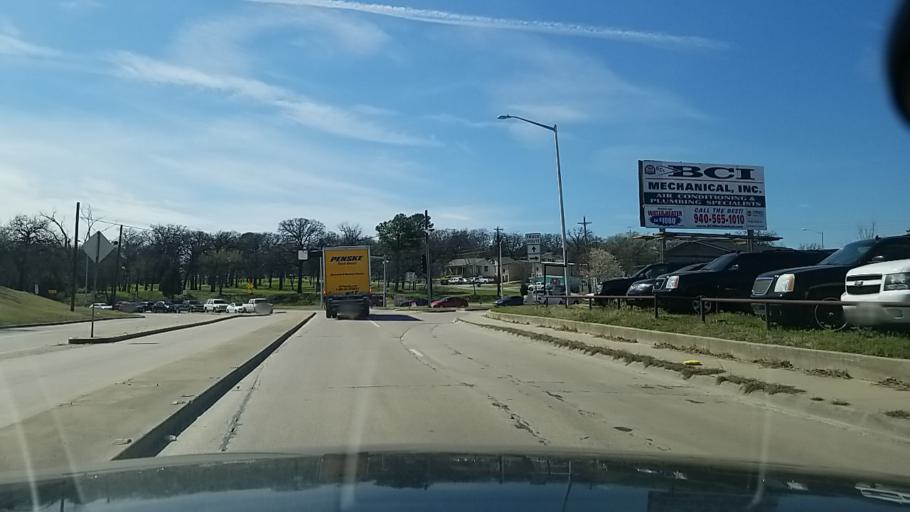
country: US
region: Texas
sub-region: Denton County
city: Denton
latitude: 33.2070
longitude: -97.1315
